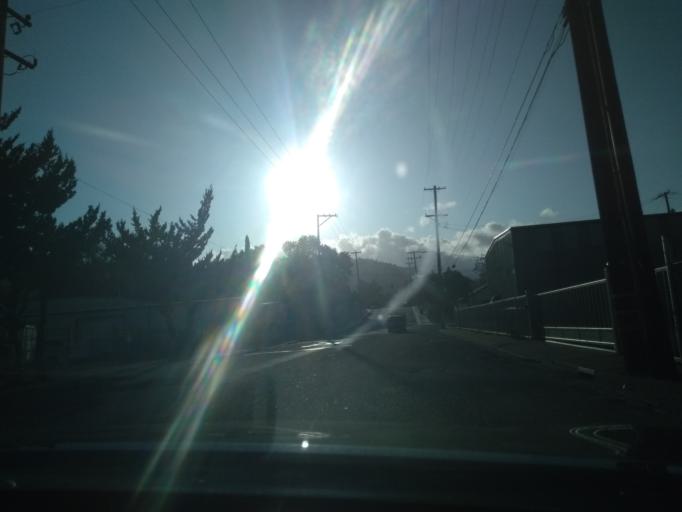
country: US
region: California
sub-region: Mendocino County
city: Ukiah
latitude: 39.1593
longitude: -123.2065
